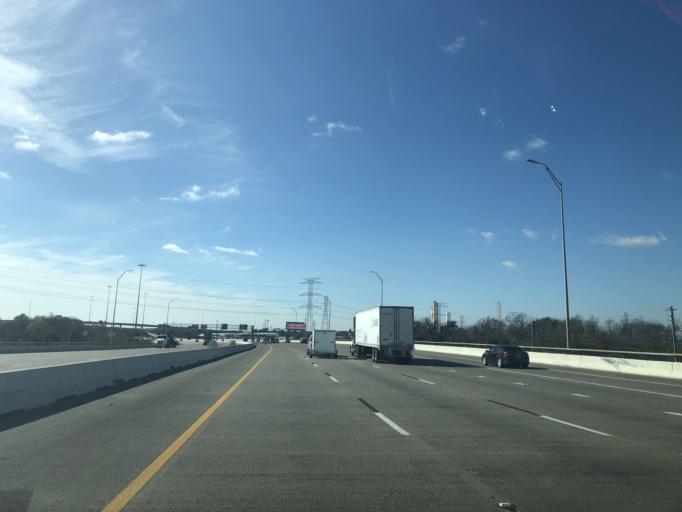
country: US
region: Texas
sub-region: Harris County
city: La Porte
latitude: 29.6965
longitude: -95.0264
